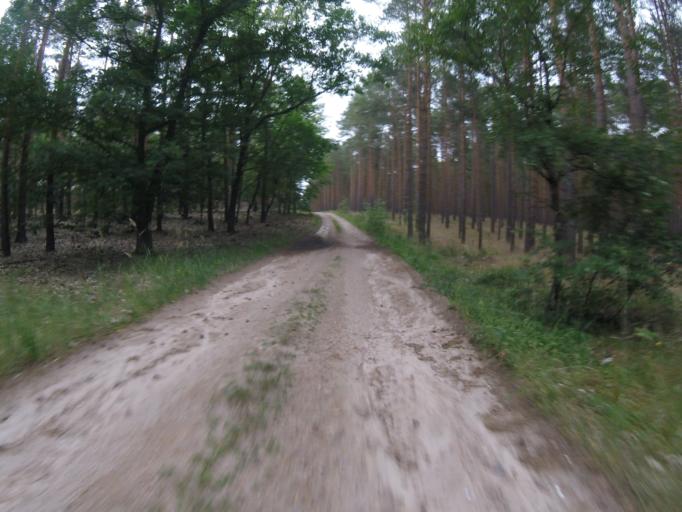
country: DE
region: Brandenburg
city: Gross Koris
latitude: 52.2098
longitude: 13.6828
